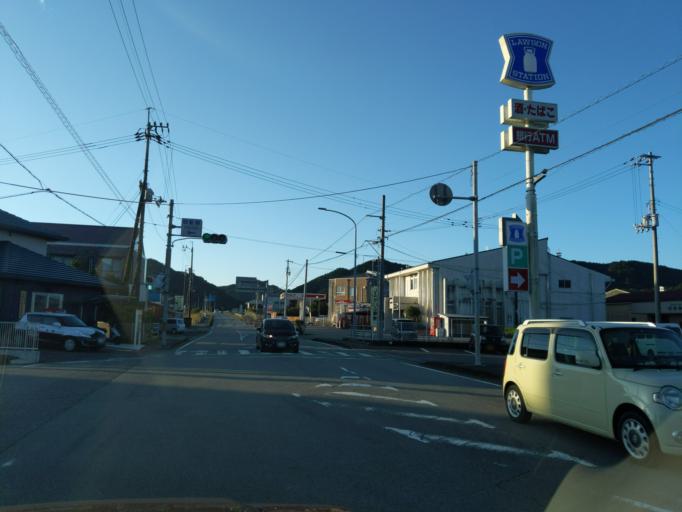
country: JP
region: Kochi
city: Muroto-misakicho
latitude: 33.6017
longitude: 134.3515
